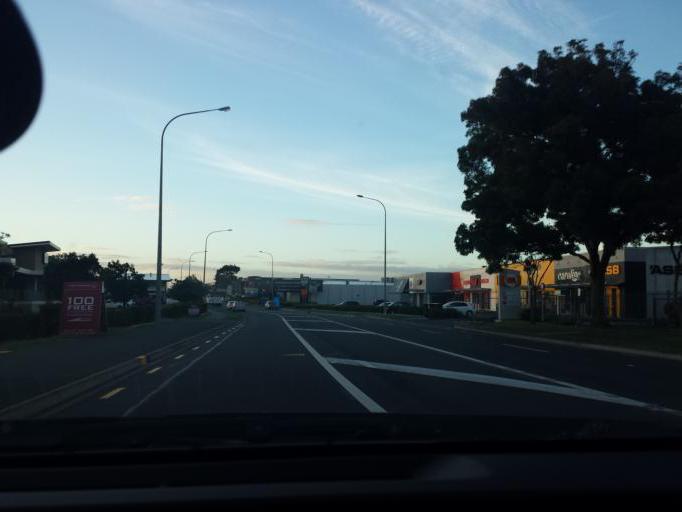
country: NZ
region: Auckland
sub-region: Auckland
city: Tamaki
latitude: -36.8899
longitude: 174.8333
